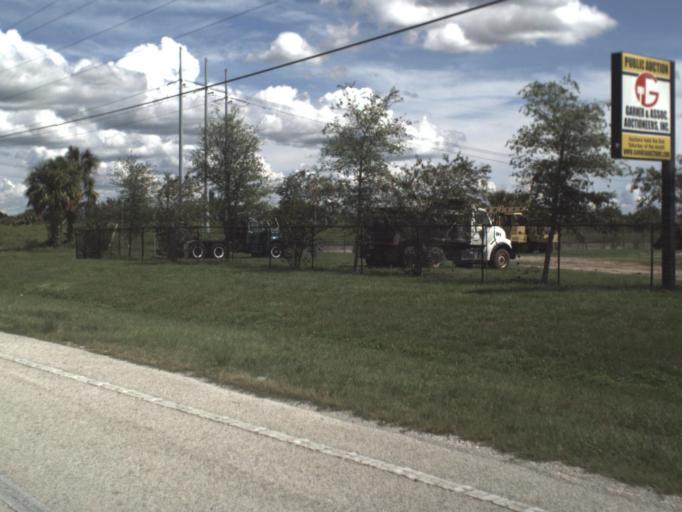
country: US
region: Florida
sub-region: Polk County
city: Mulberry
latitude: 27.8944
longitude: -81.9241
